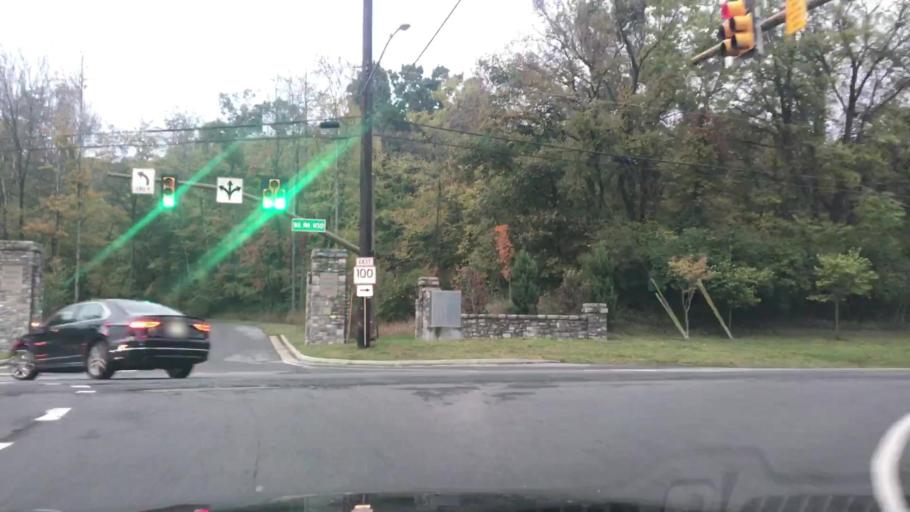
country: US
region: Tennessee
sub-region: Davidson County
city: Belle Meade
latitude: 36.0622
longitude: -86.9045
